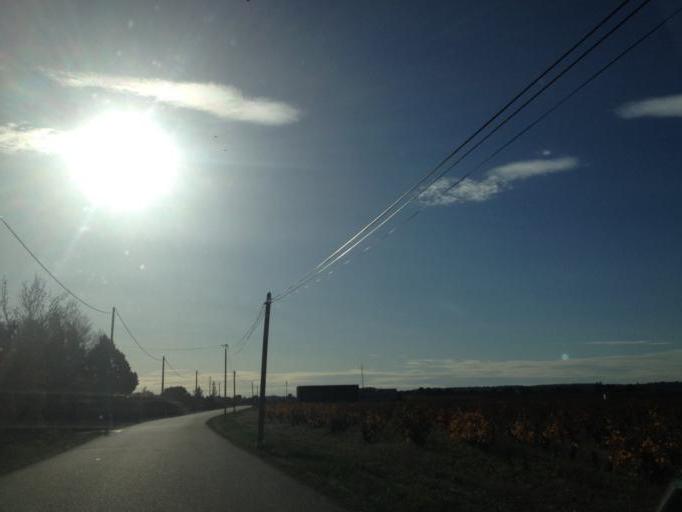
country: FR
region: Provence-Alpes-Cote d'Azur
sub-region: Departement du Vaucluse
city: Courthezon
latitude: 44.1042
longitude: 4.8774
